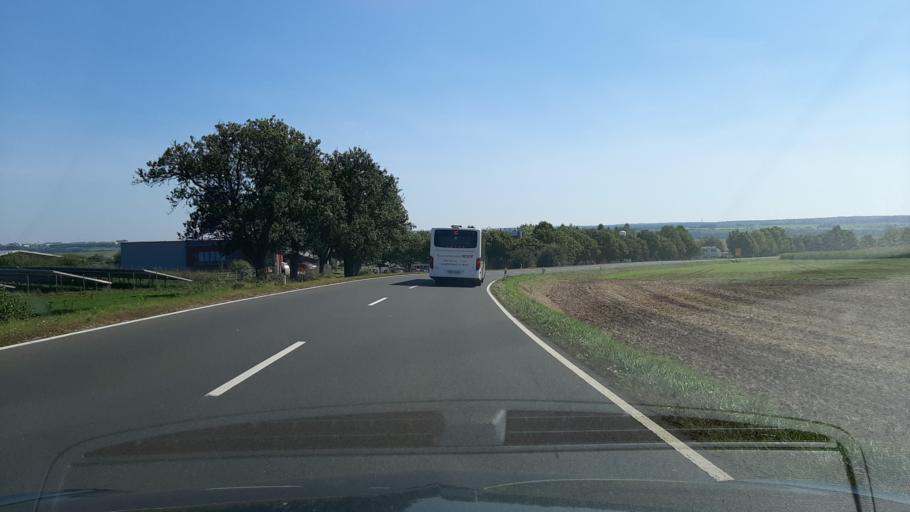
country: DE
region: Rheinland-Pfalz
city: Dudeldorf
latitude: 49.9770
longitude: 6.6251
